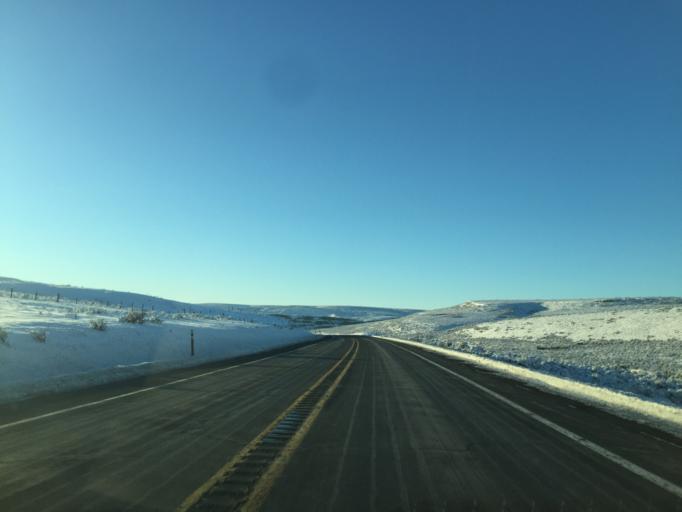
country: US
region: Washington
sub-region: Grant County
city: Soap Lake
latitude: 47.6063
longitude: -119.6418
